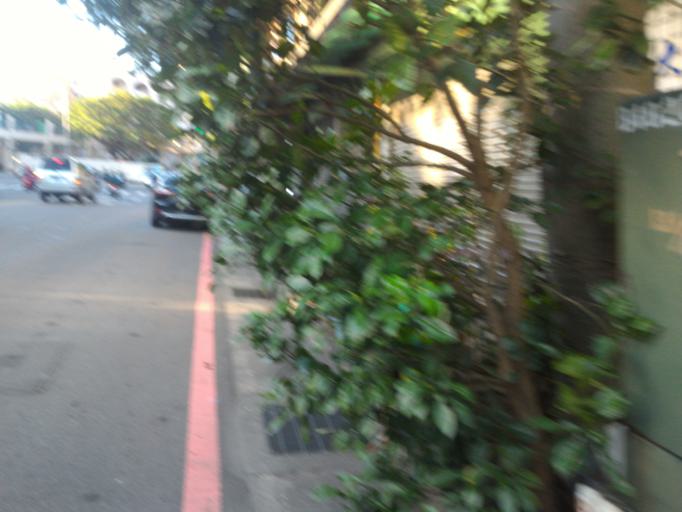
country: TW
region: Taiwan
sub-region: Taoyuan
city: Taoyuan
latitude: 24.9568
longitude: 121.3898
